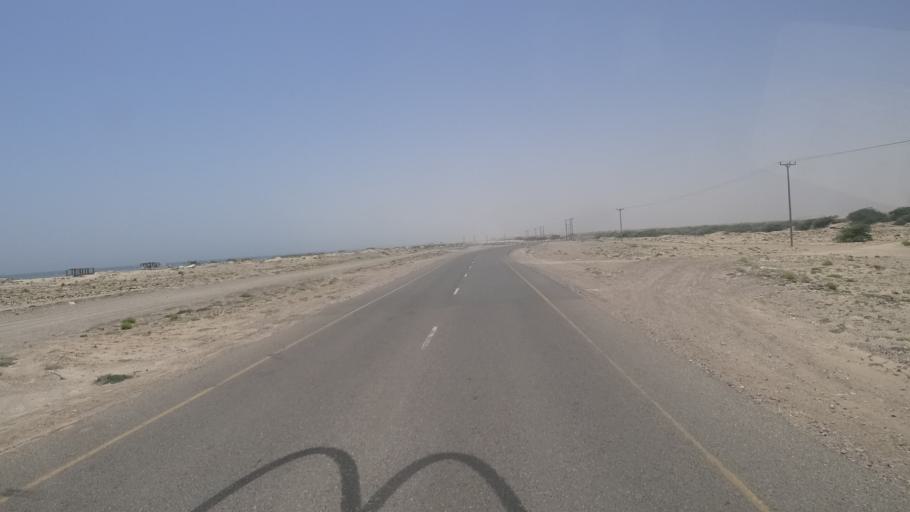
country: OM
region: Ash Sharqiyah
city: Sur
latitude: 22.0998
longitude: 59.7017
